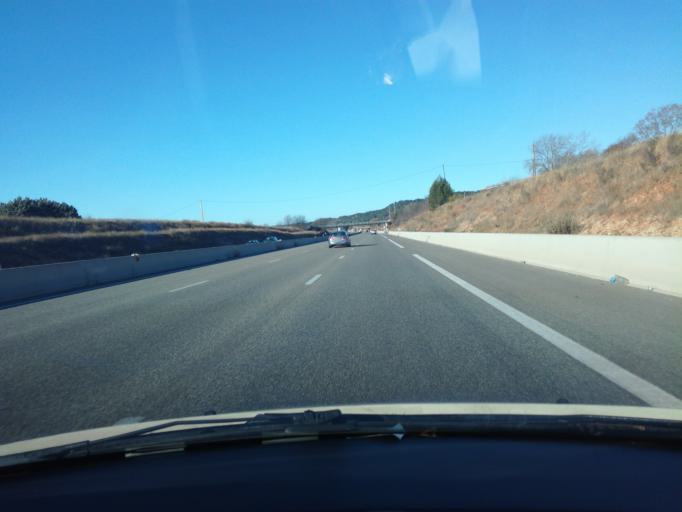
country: FR
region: Provence-Alpes-Cote d'Azur
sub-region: Departement des Bouches-du-Rhone
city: Rousset
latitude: 43.4737
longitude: 5.6314
